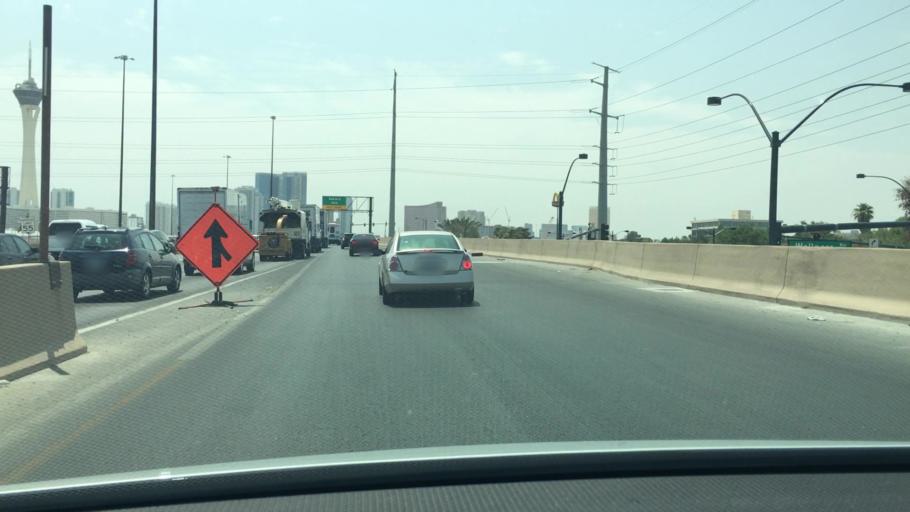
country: US
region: Nevada
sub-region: Clark County
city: Las Vegas
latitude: 36.1622
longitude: -115.1616
